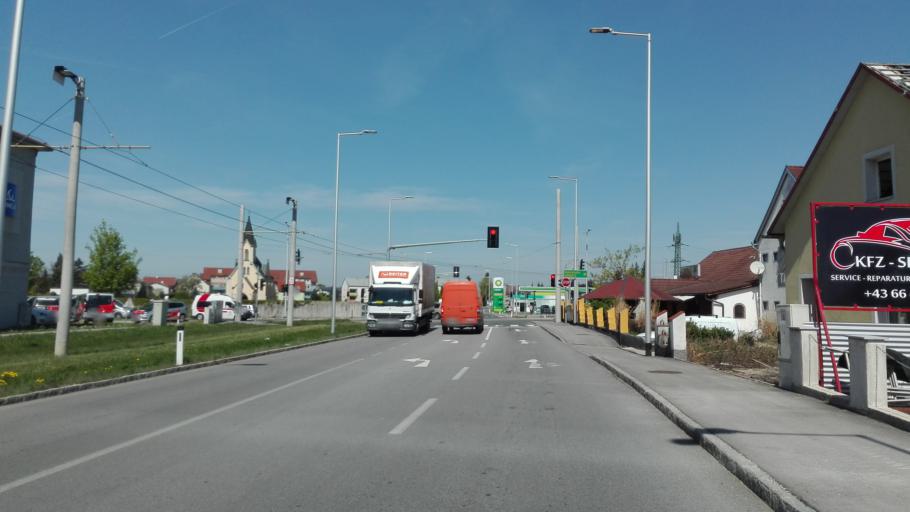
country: AT
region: Upper Austria
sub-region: Politischer Bezirk Linz-Land
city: Traun
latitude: 48.2257
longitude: 14.2348
